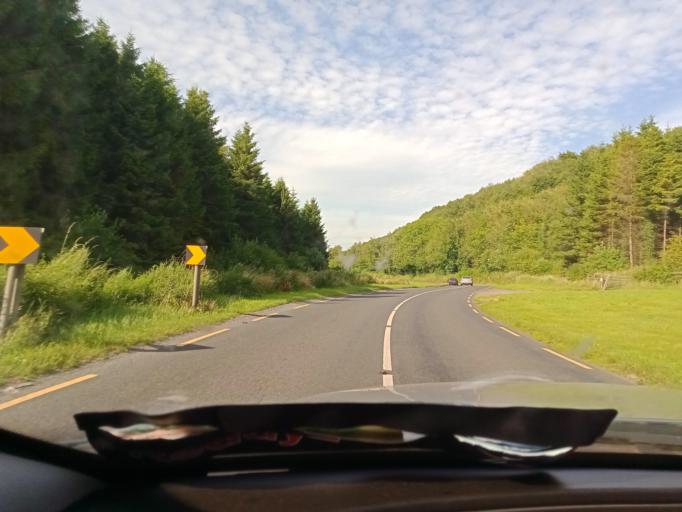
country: IE
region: Leinster
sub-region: An Iarmhi
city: Castlepollard
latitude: 53.5935
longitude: -7.3012
